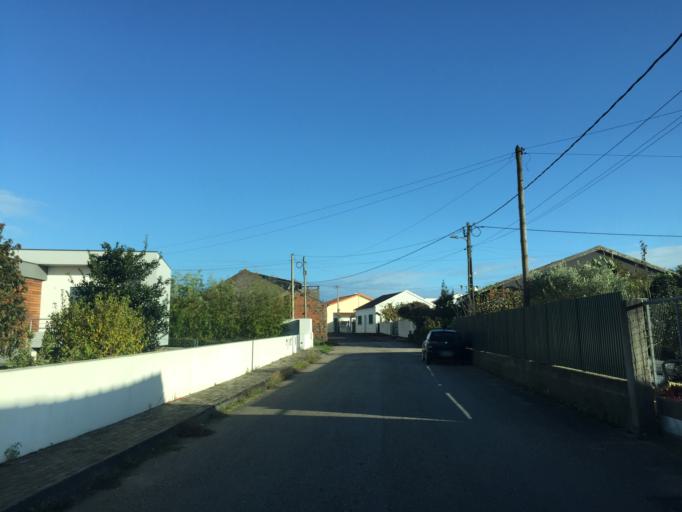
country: PT
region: Coimbra
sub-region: Figueira da Foz
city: Lavos
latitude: 40.0555
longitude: -8.8091
